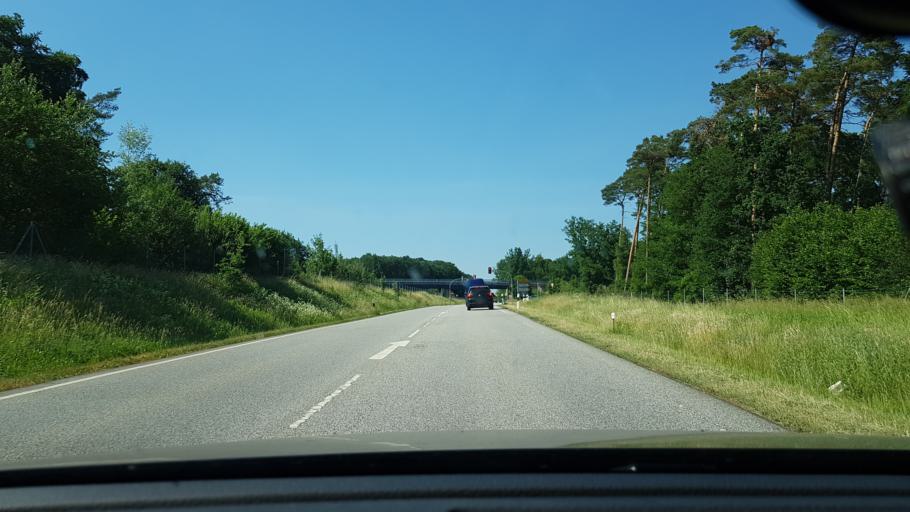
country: DE
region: Schleswig-Holstein
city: Gross Sarau
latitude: 53.7912
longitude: 10.7021
